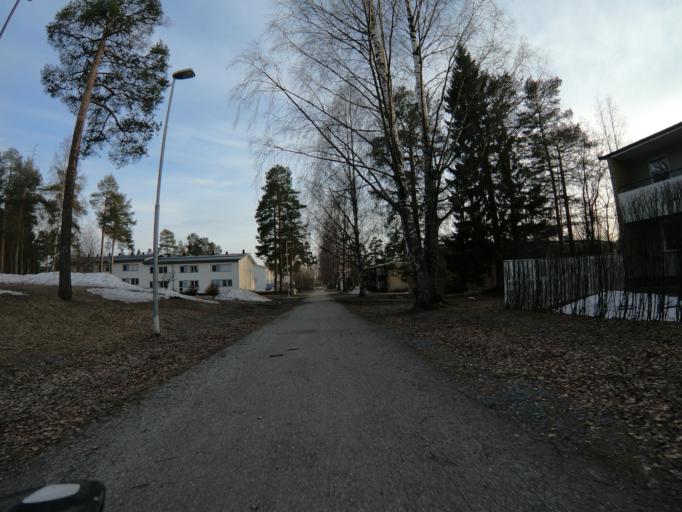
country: SE
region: Vaesterbotten
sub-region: Umea Kommun
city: Umea
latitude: 63.8411
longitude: 20.2795
